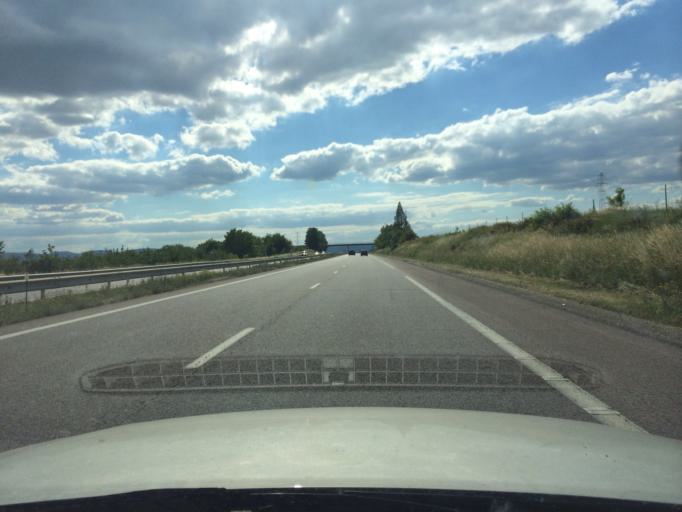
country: FR
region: Alsace
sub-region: Departement du Bas-Rhin
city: Hochfelden
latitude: 48.7700
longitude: 7.5274
